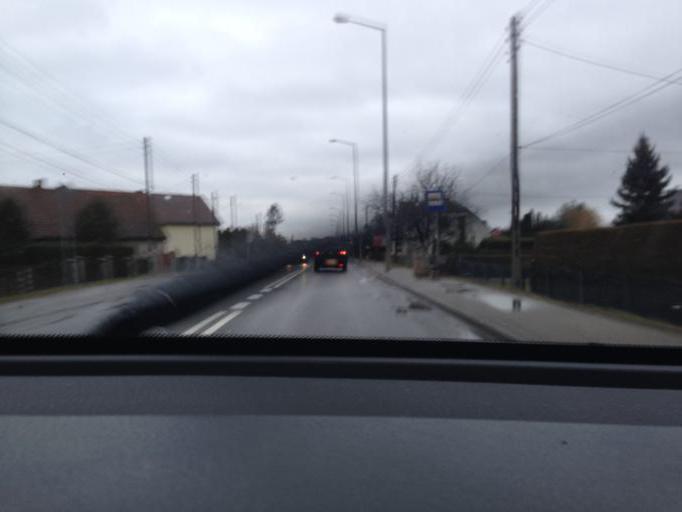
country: PL
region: Opole Voivodeship
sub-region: Powiat opolski
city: Opole
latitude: 50.6960
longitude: 17.9569
